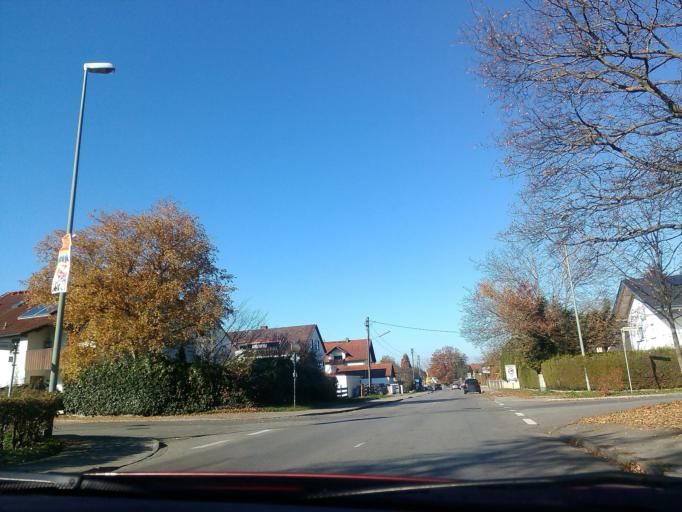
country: DE
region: Bavaria
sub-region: Upper Bavaria
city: Olching
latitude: 48.2025
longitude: 11.3309
